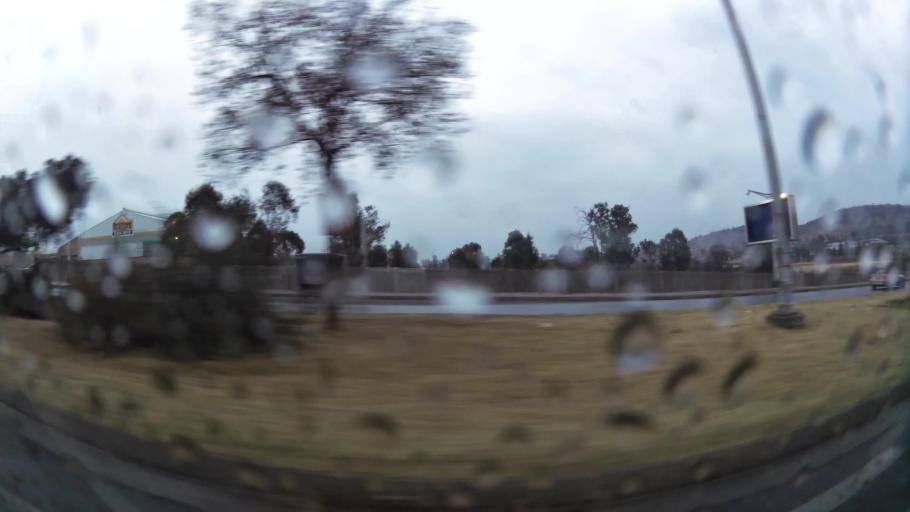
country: ZA
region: Gauteng
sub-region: City of Johannesburg Metropolitan Municipality
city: Soweto
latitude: -26.2593
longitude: 27.9276
